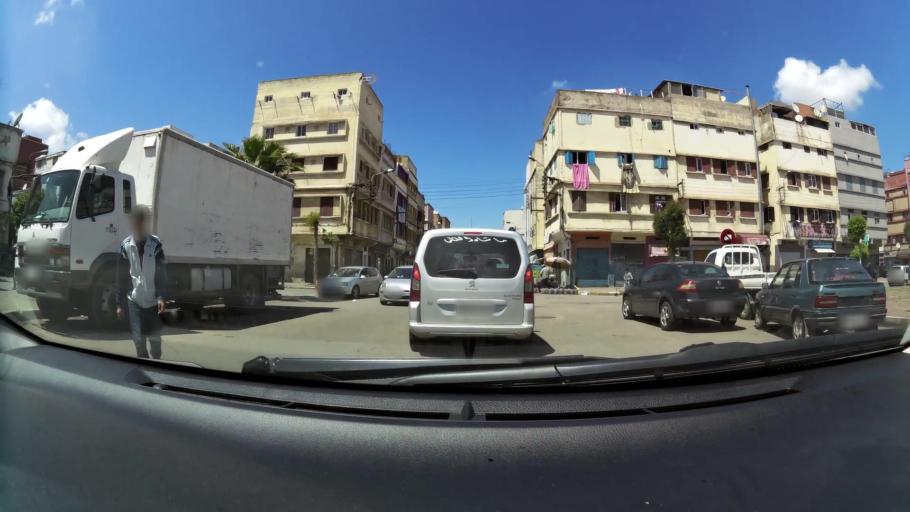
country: MA
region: Grand Casablanca
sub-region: Casablanca
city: Casablanca
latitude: 33.5640
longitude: -7.5739
